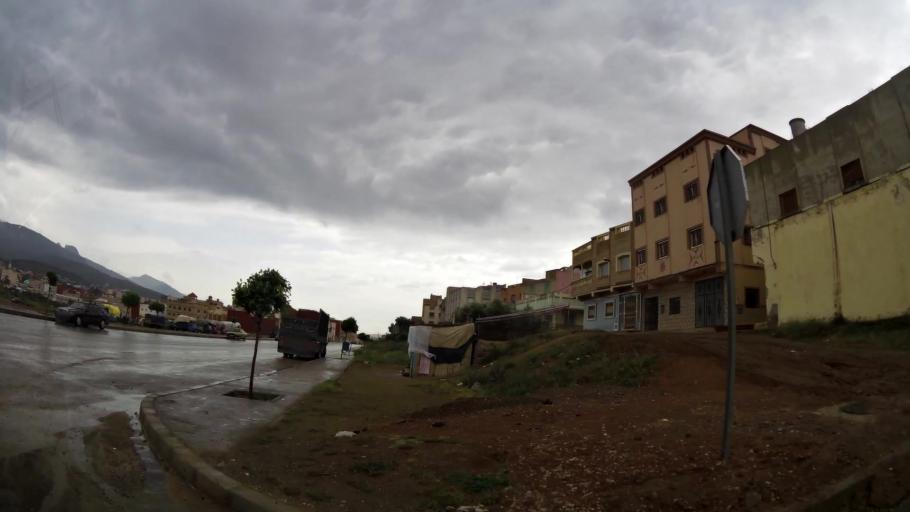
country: MA
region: Oriental
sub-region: Nador
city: Nador
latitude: 35.1480
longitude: -3.0044
